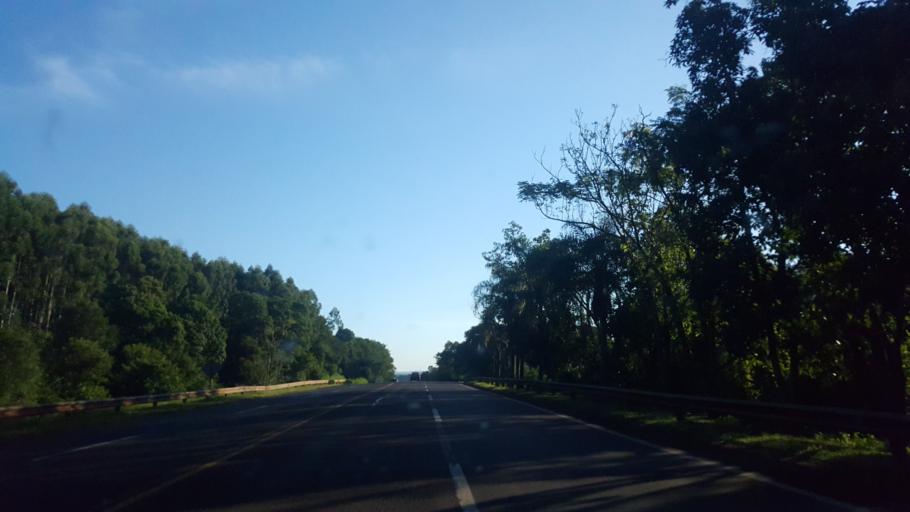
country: AR
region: Misiones
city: El Alcazar
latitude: -26.7255
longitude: -54.8668
